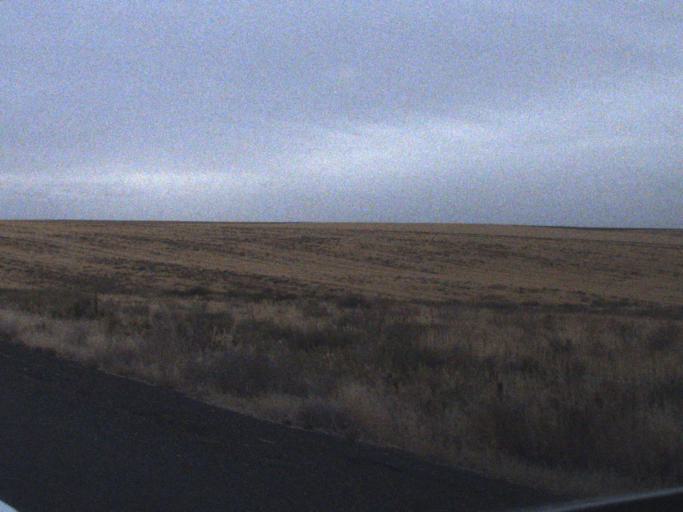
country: US
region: Washington
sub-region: Franklin County
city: Connell
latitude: 46.7942
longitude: -118.7210
